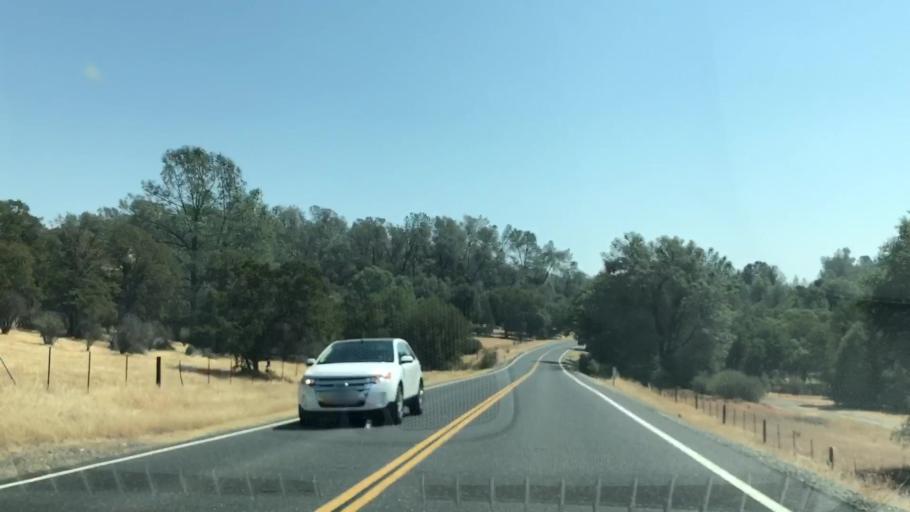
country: US
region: California
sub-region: Calaveras County
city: Copperopolis
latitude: 37.9507
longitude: -120.6126
